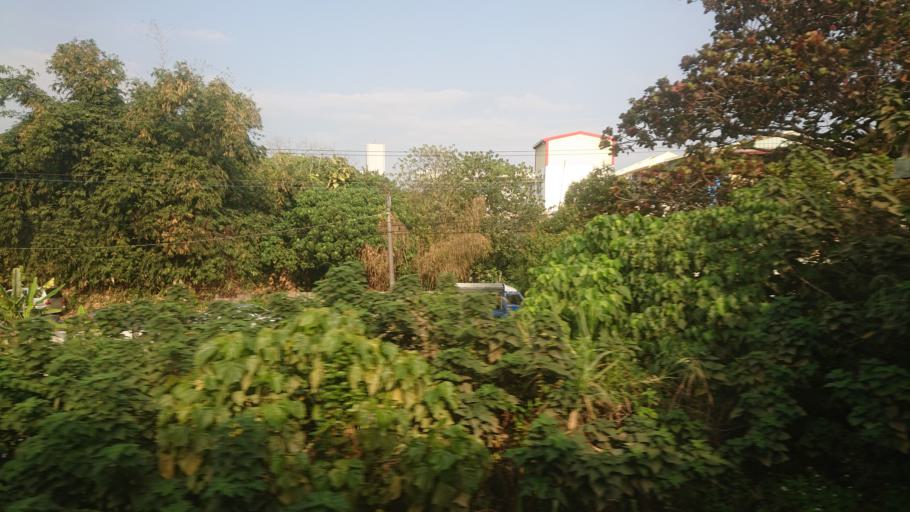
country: TW
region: Taiwan
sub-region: Yunlin
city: Douliu
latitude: 23.7090
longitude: 120.5368
